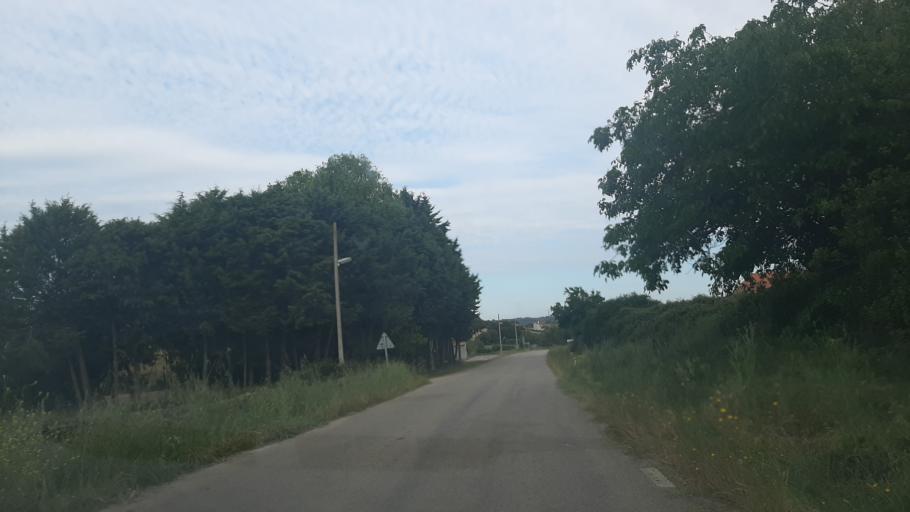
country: ES
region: Castille and Leon
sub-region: Provincia de Salamanca
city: Gallegos de Arganan
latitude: 40.6470
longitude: -6.7525
